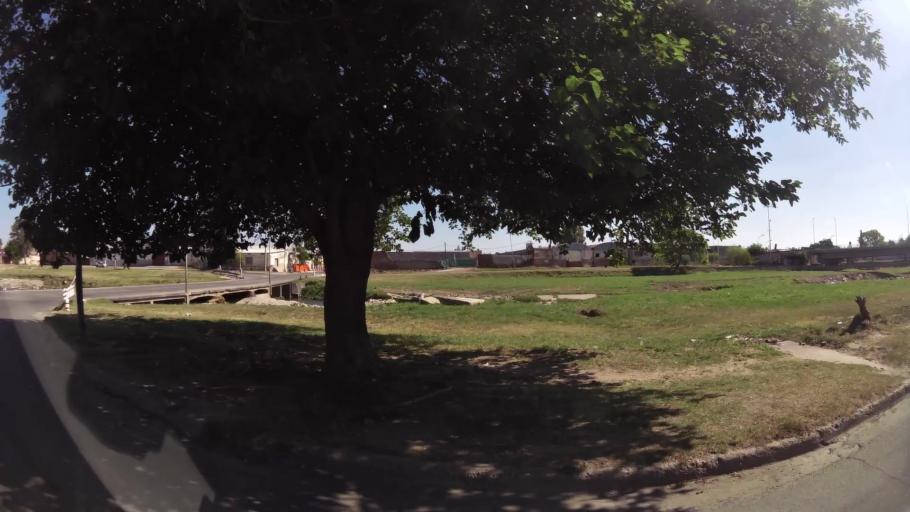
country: AR
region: Cordoba
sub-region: Departamento de Capital
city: Cordoba
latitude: -31.4179
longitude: -64.1501
